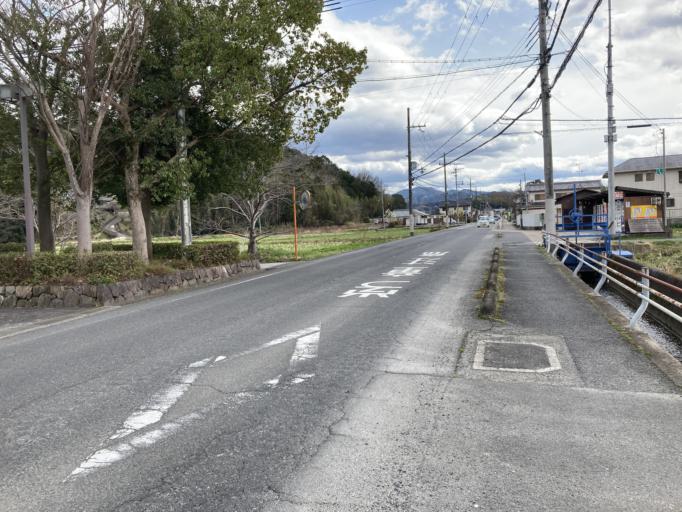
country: JP
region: Nara
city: Kashihara-shi
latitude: 34.4974
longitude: 135.8145
